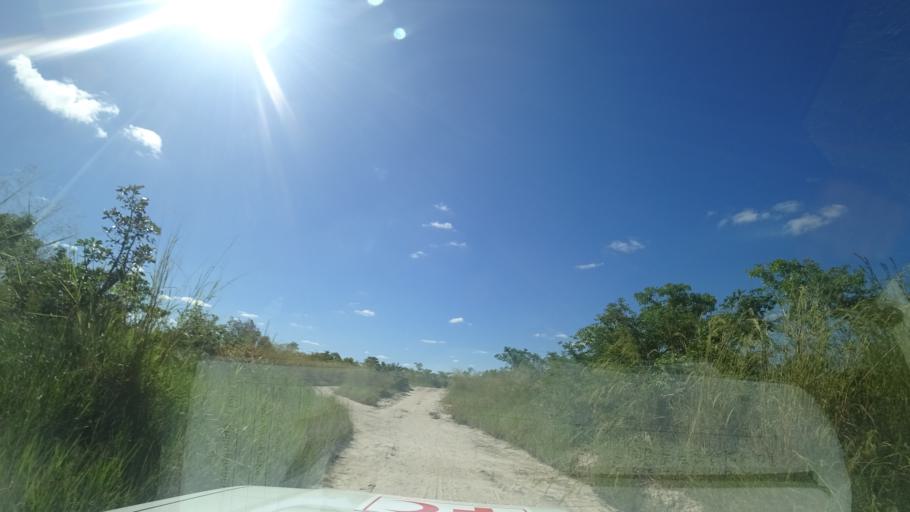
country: MZ
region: Sofala
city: Dondo
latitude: -19.4802
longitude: 34.6261
